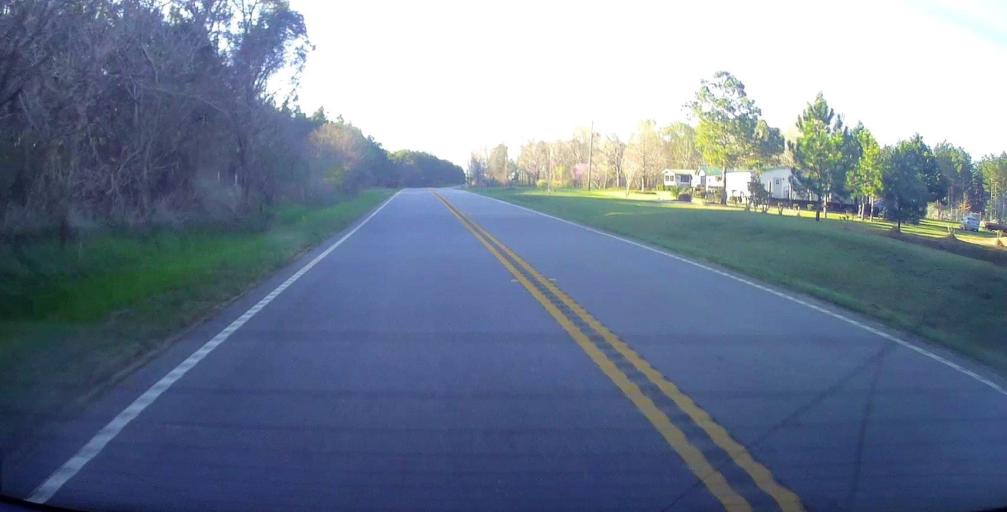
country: US
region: Georgia
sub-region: Pulaski County
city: Hawkinsville
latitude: 32.1820
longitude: -83.3629
